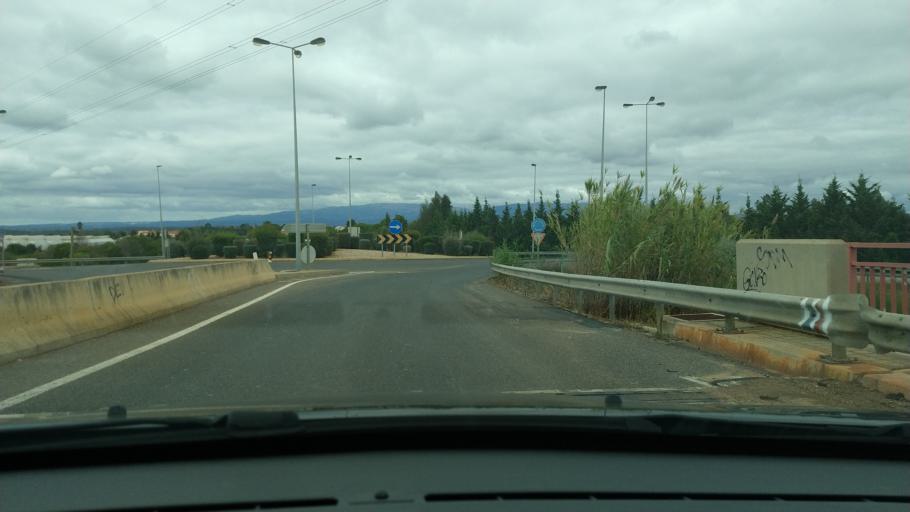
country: PT
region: Faro
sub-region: Lagoa
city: Lagoa
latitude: 37.1452
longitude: -8.4546
